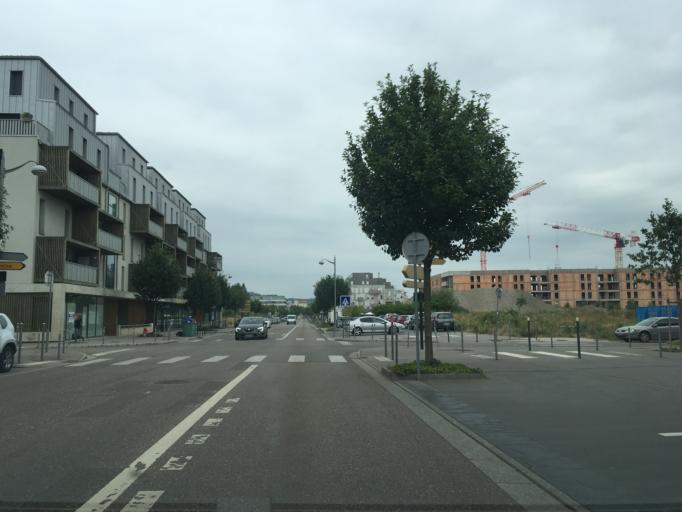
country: FR
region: Lorraine
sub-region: Departement de Meurthe-et-Moselle
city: Tomblaine
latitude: 48.6897
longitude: 6.2006
